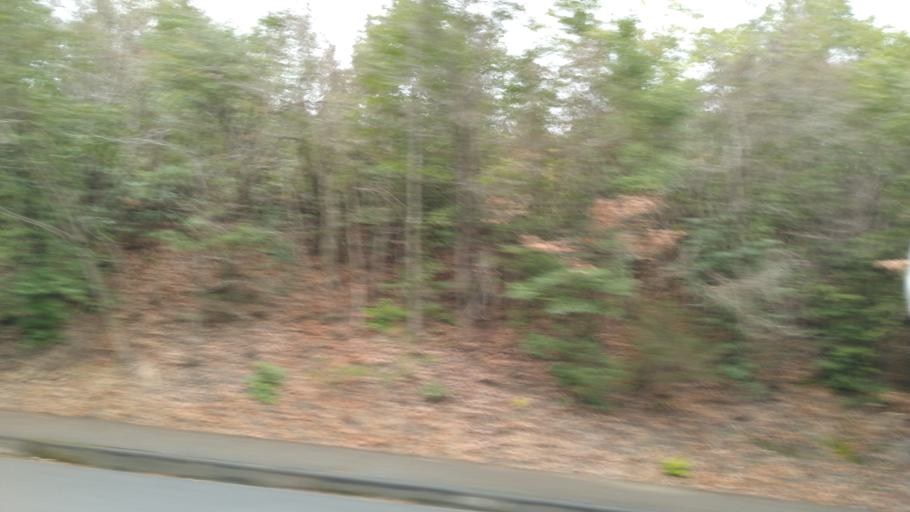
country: JP
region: Kyoto
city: Fukuchiyama
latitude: 35.2919
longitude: 135.1593
